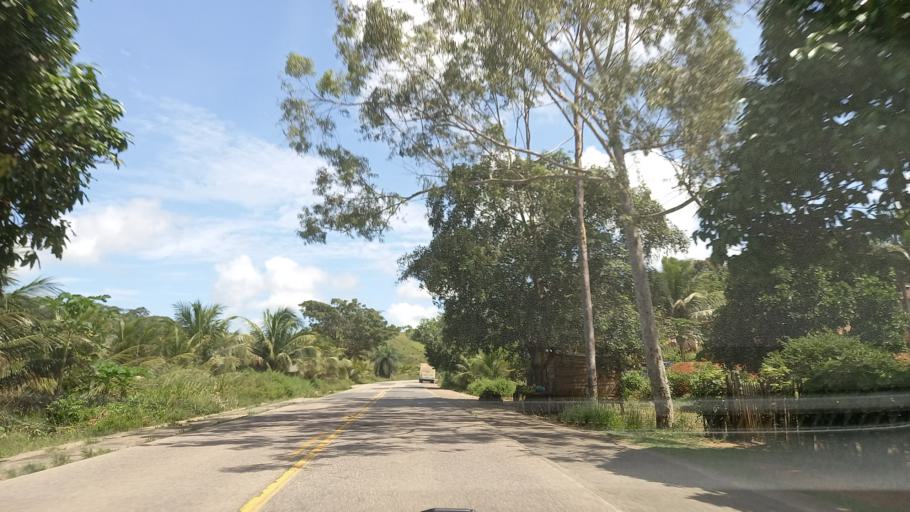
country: BR
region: Pernambuco
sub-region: Barreiros
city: Barreiros
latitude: -8.7791
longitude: -35.1746
